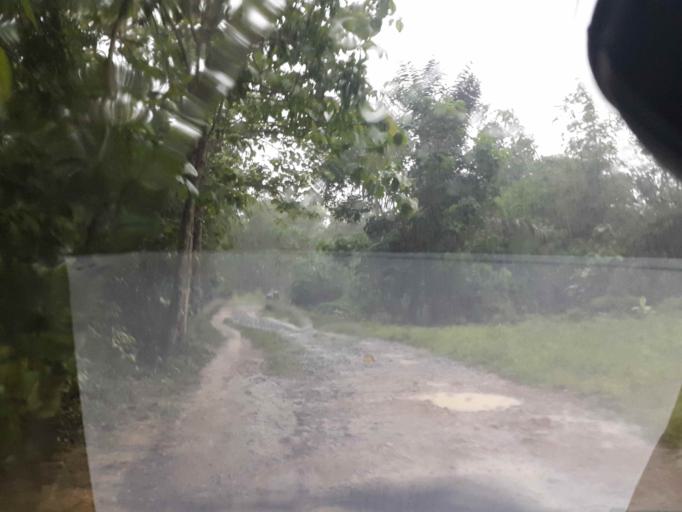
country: ID
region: Lampung
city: Kedaton
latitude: -5.3922
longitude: 105.3373
